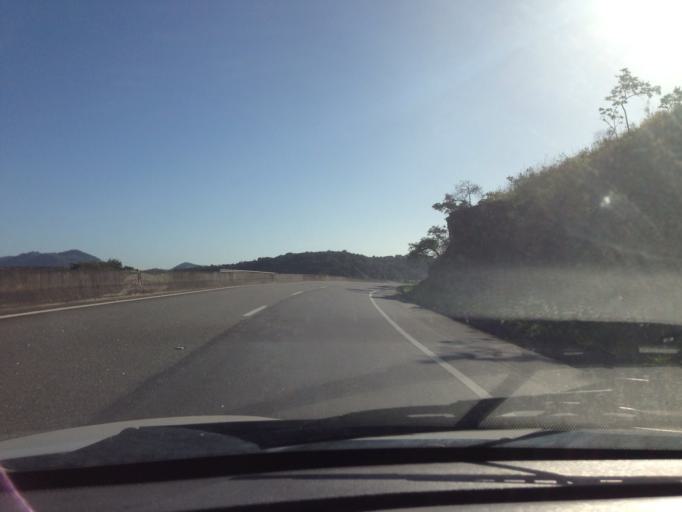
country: BR
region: Espirito Santo
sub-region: Guarapari
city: Guarapari
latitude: -20.6185
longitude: -40.4942
